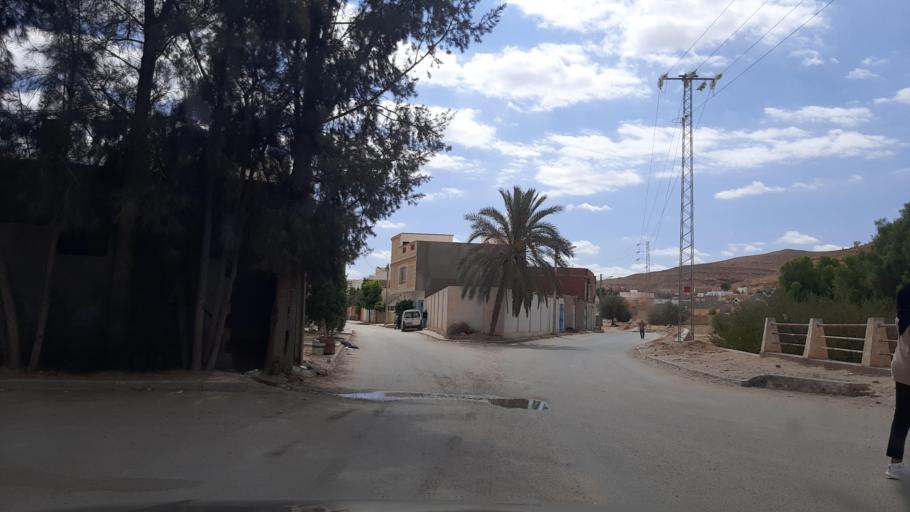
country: TN
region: Tataouine
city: Tataouine
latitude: 32.9284
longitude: 10.4581
